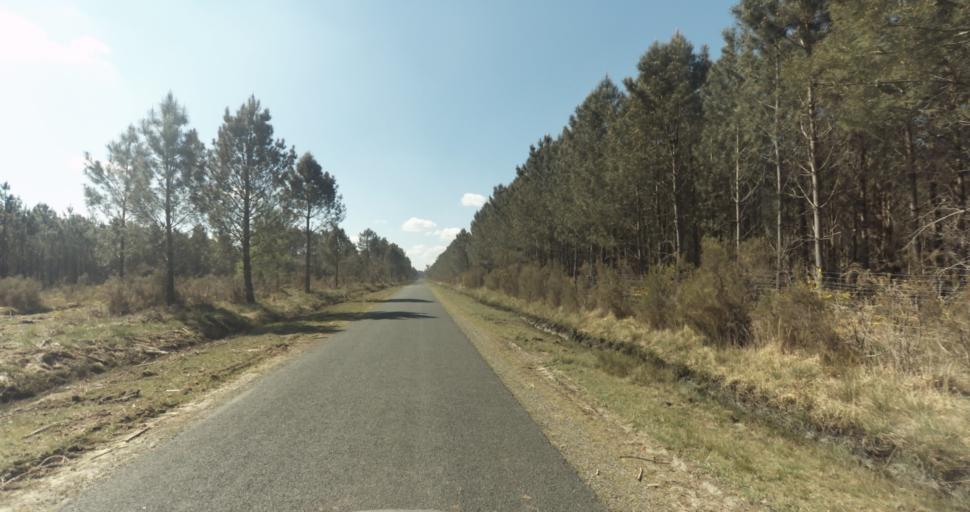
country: FR
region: Aquitaine
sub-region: Departement de la Gironde
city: Martignas-sur-Jalle
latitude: 44.7815
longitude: -0.8019
